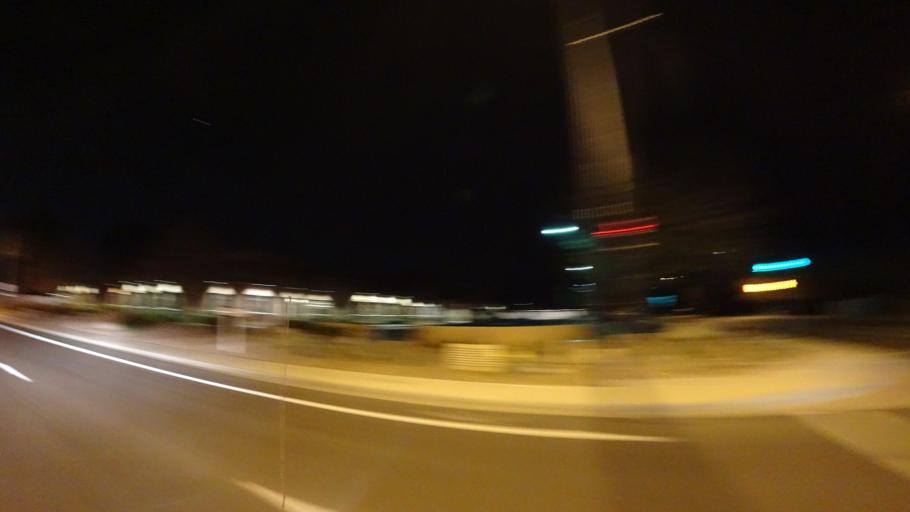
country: US
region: Arizona
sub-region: Maricopa County
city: Mesa
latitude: 33.4517
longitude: -111.7964
